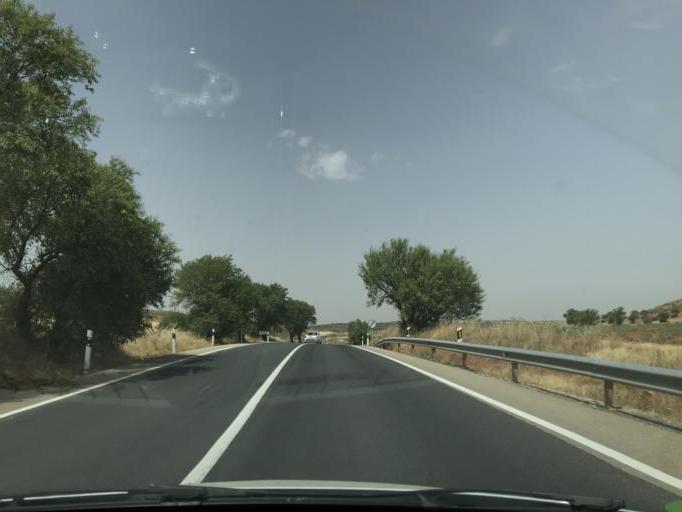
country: ES
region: Castille-La Mancha
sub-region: Provincia de Cuenca
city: Villar de Domingo Garcia
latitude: 40.2433
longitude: -2.2966
